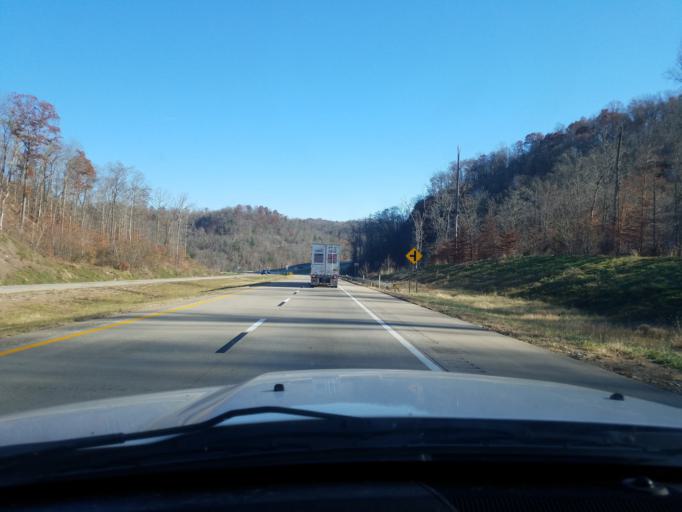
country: US
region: West Virginia
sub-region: Putnam County
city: Eleanor
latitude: 38.5269
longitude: -81.9410
